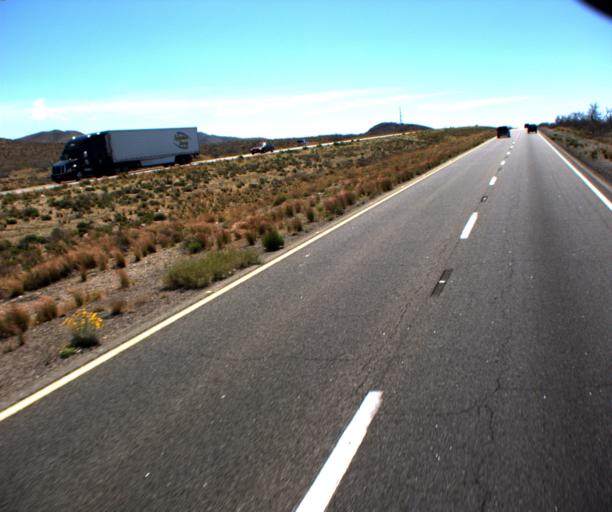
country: US
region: Arizona
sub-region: Mohave County
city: Dolan Springs
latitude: 35.4487
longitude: -114.2967
